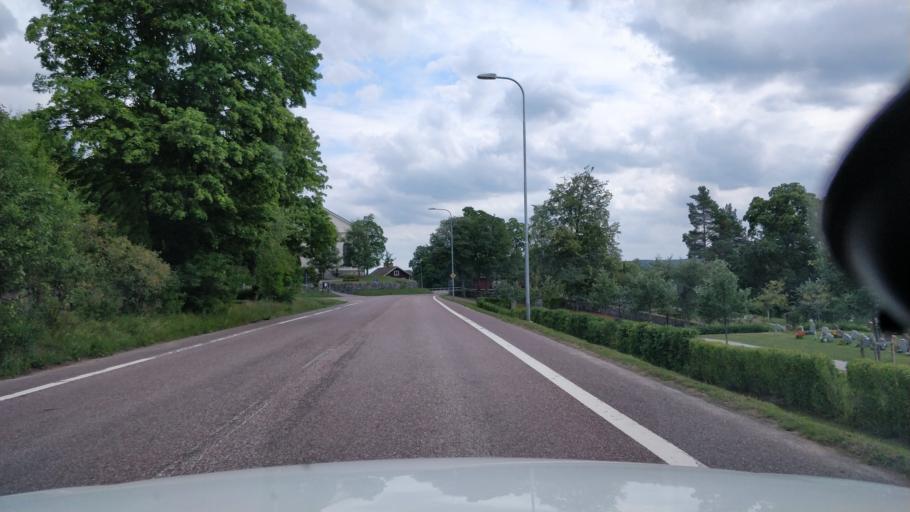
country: SE
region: Dalarna
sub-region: Faluns Kommun
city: Bjursas
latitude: 60.7382
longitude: 15.4476
